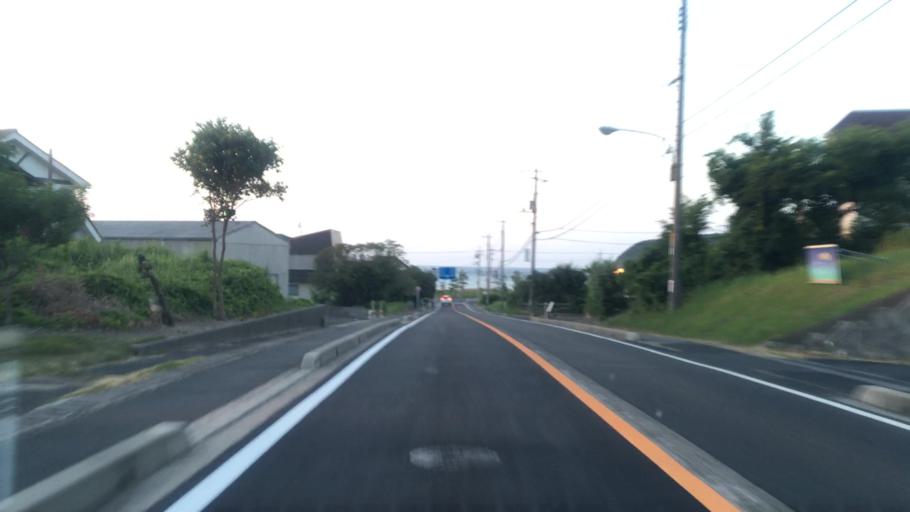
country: JP
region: Tottori
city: Tottori
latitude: 35.5888
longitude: 134.3326
